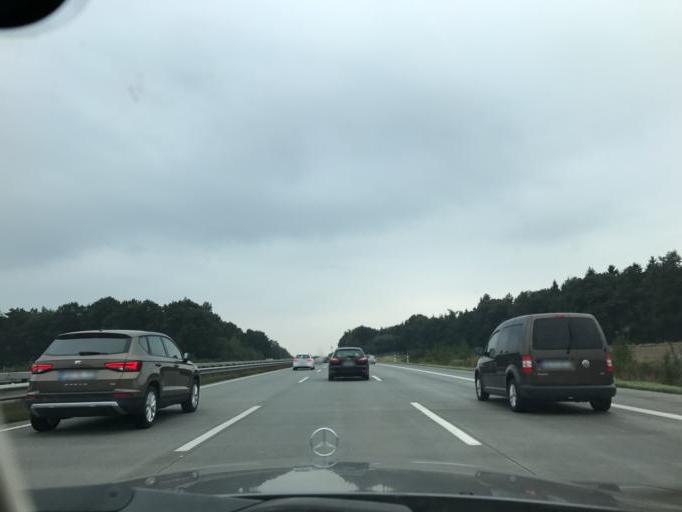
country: DE
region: Lower Saxony
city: Horstedt
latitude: 53.1602
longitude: 9.2399
